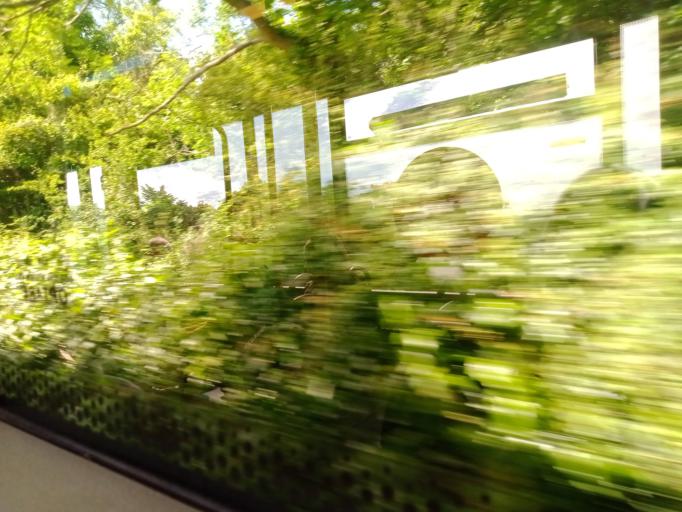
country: GB
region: Wales
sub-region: Anglesey
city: Llangoed
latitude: 53.2999
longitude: -4.0746
